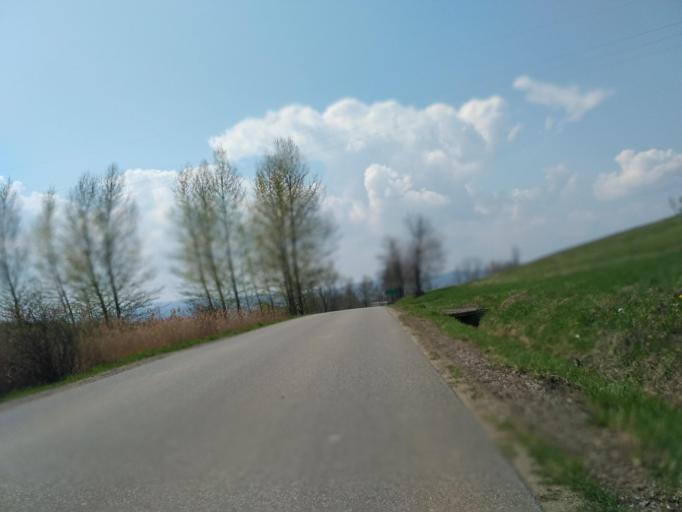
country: PL
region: Subcarpathian Voivodeship
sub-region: Powiat sanocki
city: Zarszyn
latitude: 49.5522
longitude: 21.9890
